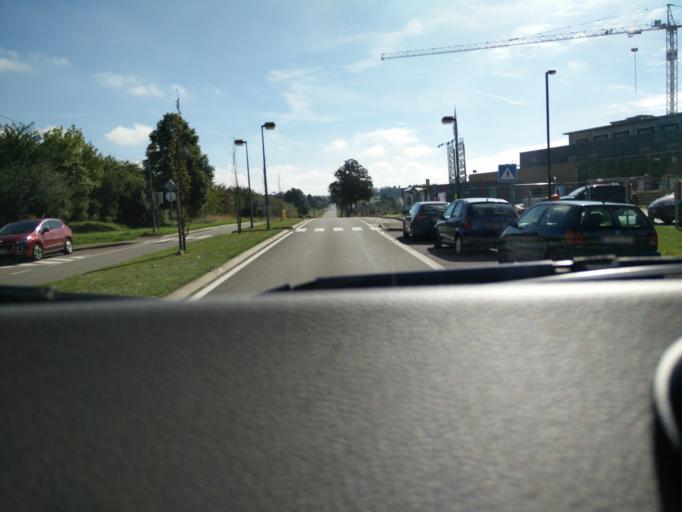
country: BE
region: Wallonia
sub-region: Province de Namur
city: Dinant
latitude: 50.2656
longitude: 4.9440
